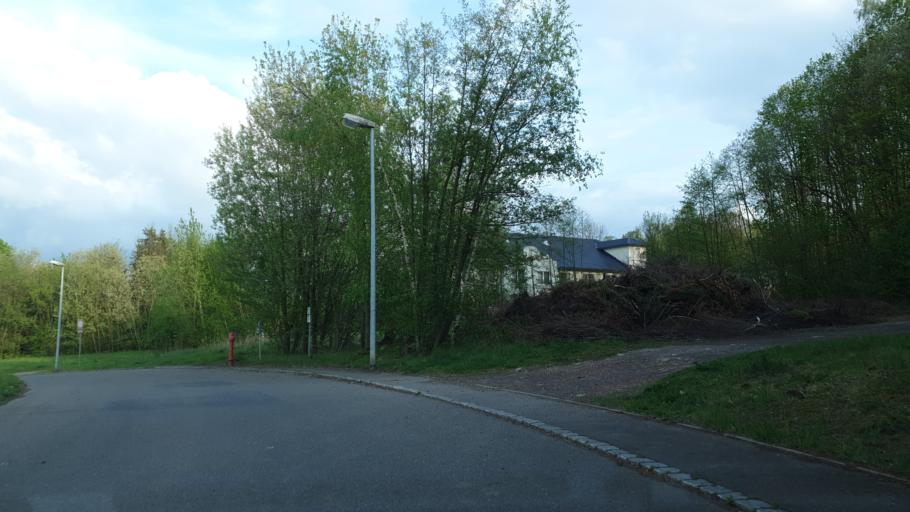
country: DE
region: Saxony
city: Oelsnitz
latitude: 50.7276
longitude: 12.6940
